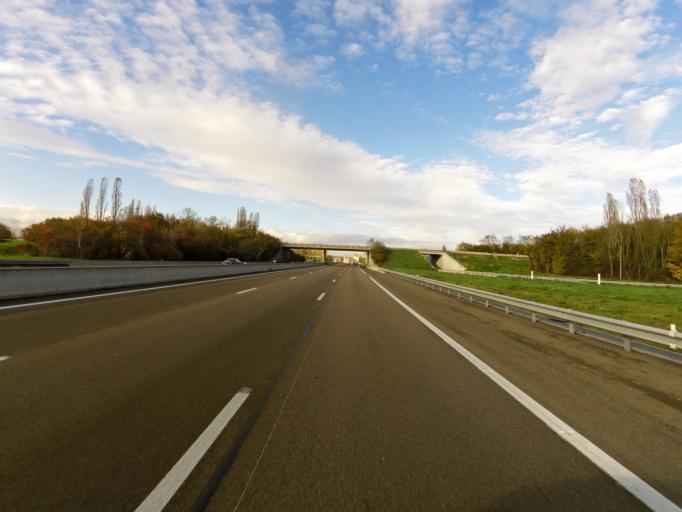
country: FR
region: Bourgogne
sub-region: Departement de la Cote-d'Or
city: Couternon
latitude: 47.3439
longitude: 5.1642
